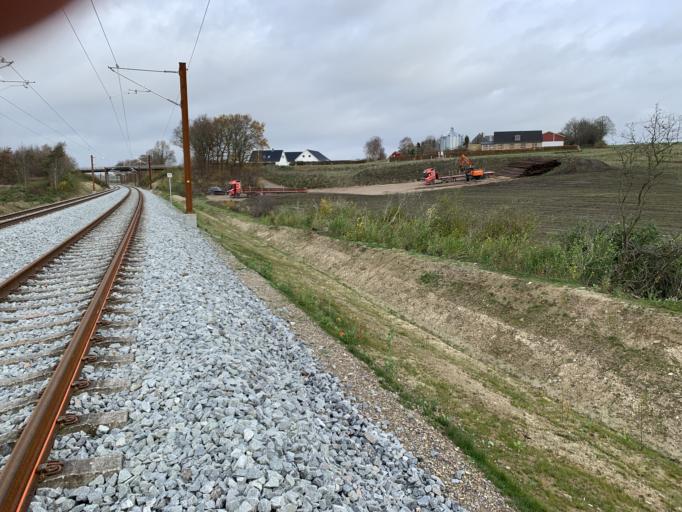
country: DK
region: Zealand
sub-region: Naestved Kommune
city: Fensmark
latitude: 55.3182
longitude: 11.7441
